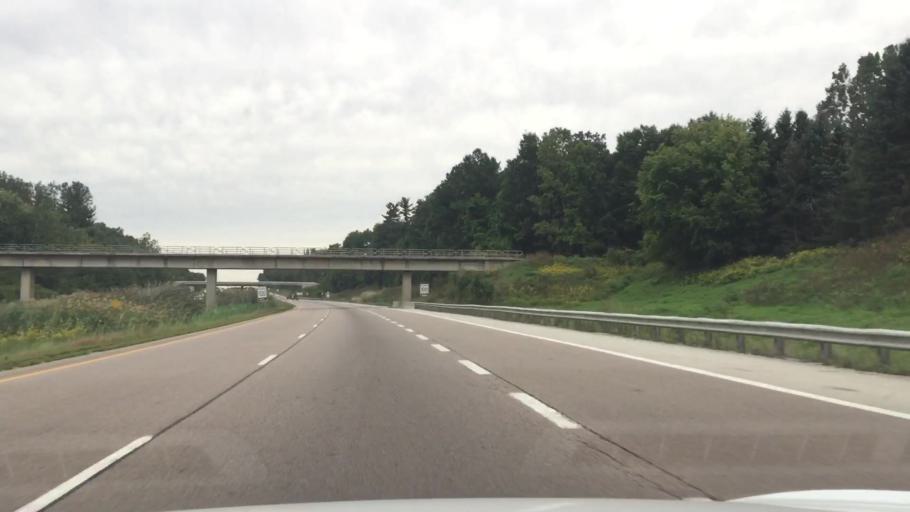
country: CA
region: Ontario
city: Delaware
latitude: 42.9256
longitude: -81.4658
